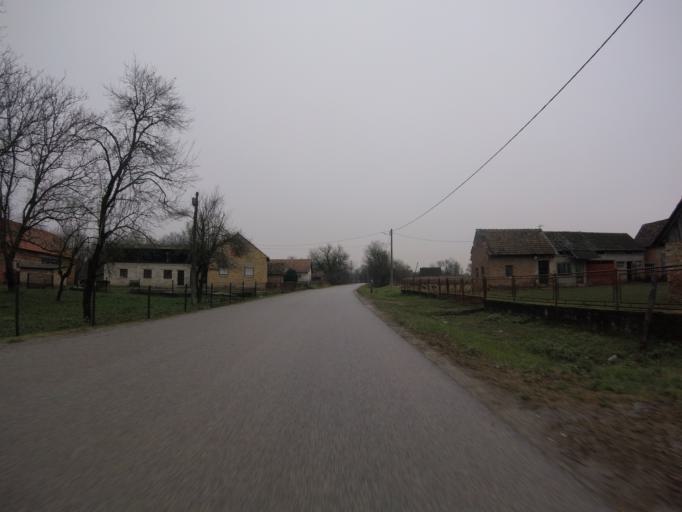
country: HR
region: Sisacko-Moslavacka
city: Lekenik
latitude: 45.6317
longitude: 16.3093
